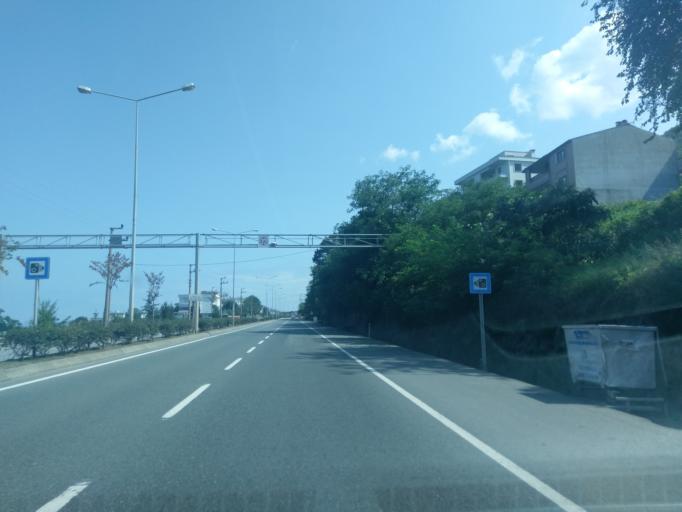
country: TR
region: Ordu
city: Ordu
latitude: 41.0157
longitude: 37.8578
